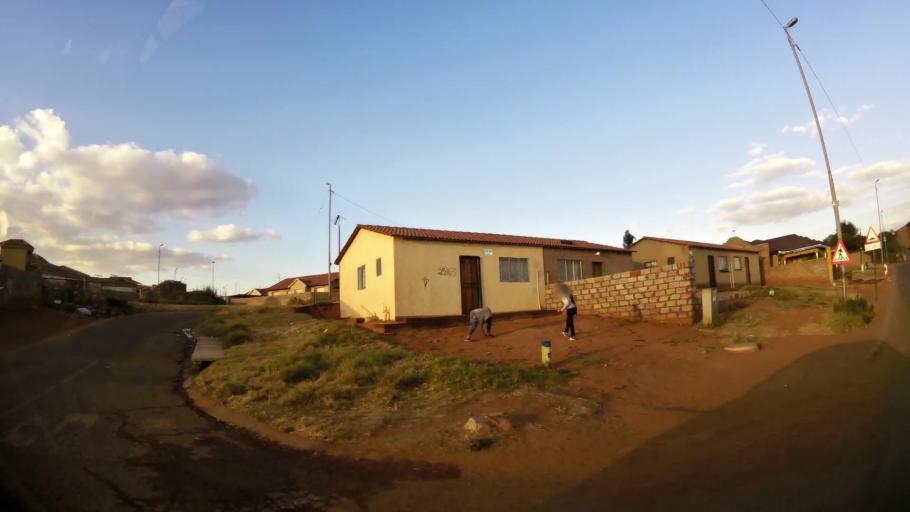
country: ZA
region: Gauteng
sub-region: West Rand District Municipality
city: Krugersdorp
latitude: -26.0770
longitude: 27.7540
